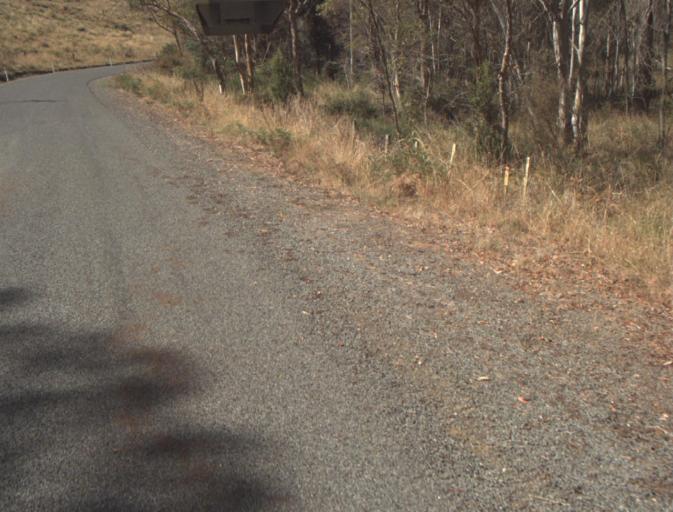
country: AU
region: Tasmania
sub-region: Launceston
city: Newstead
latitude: -41.3630
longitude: 147.3037
